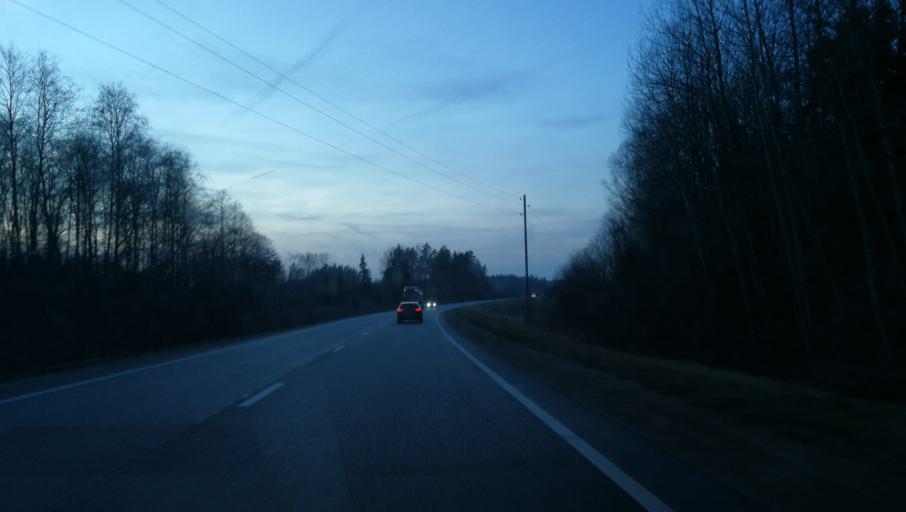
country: LV
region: Skrunda
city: Skrunda
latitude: 56.6766
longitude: 22.1571
